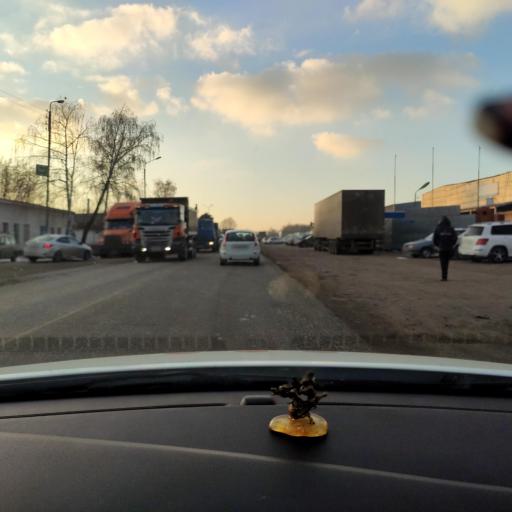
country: RU
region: Tatarstan
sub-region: Gorod Kazan'
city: Kazan
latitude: 55.7301
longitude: 49.1202
